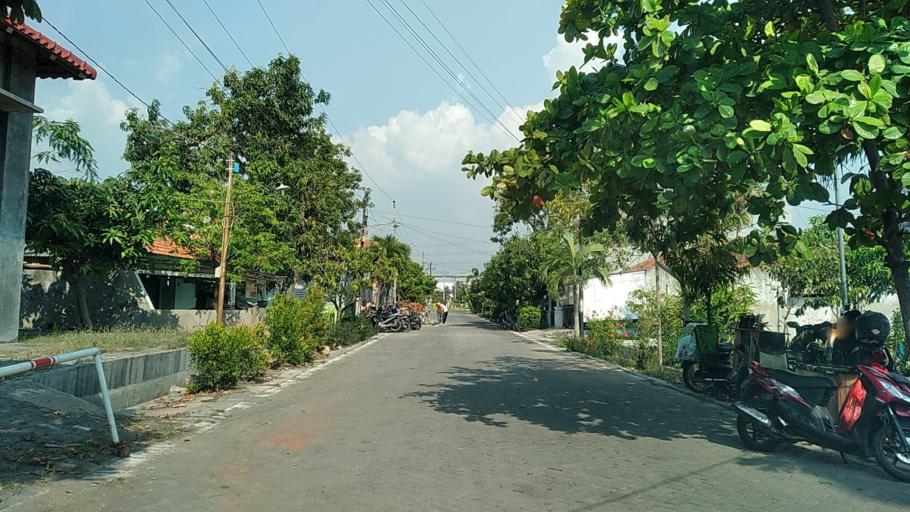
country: ID
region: Central Java
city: Semarang
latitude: -7.0002
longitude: 110.4627
